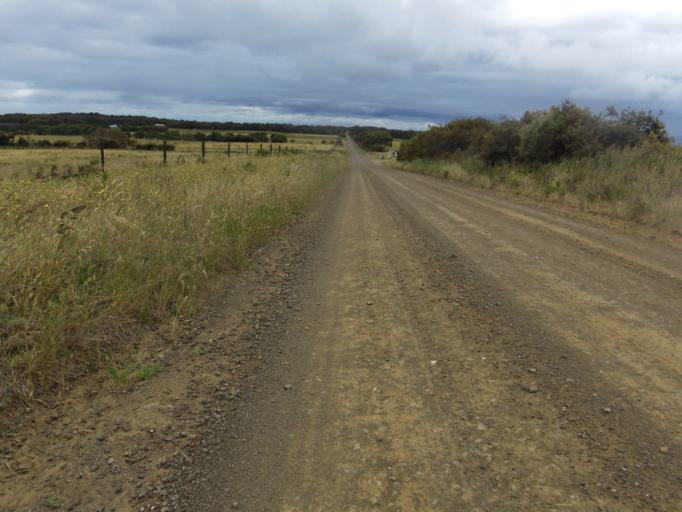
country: AU
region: Victoria
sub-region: Bass Coast
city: Cowes
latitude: -38.3813
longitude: 145.3506
